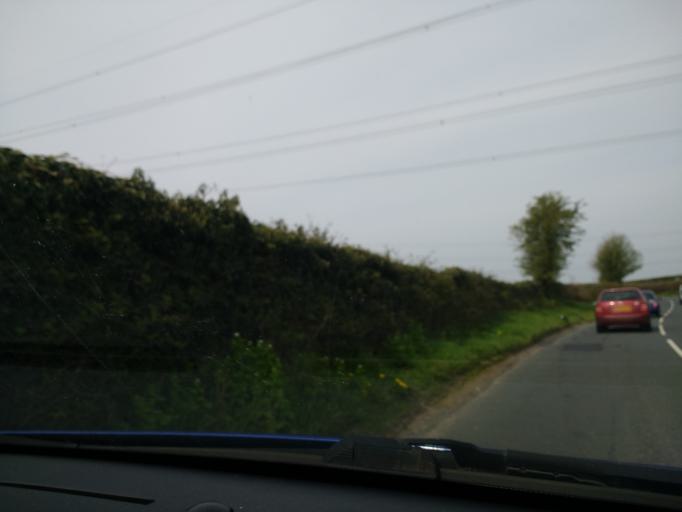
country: GB
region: England
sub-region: Lancashire
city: Lancaster
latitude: 54.0160
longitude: -2.8125
